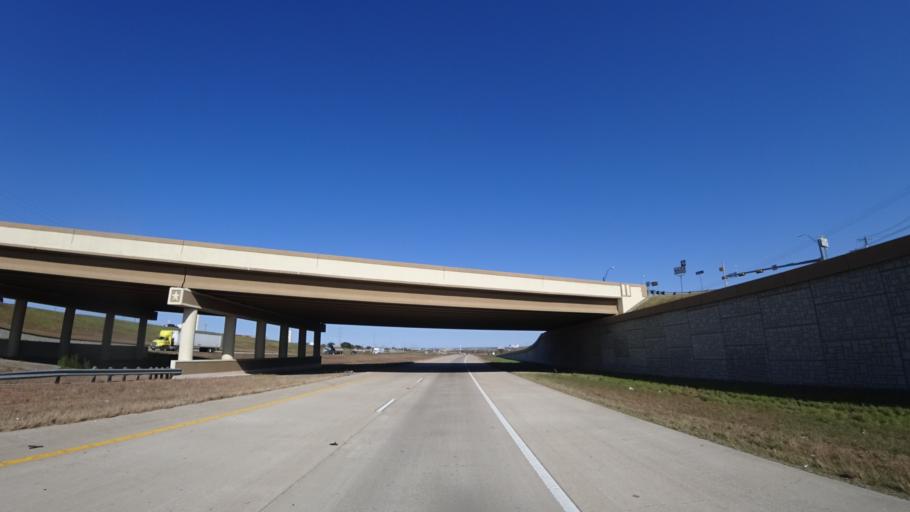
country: US
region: Texas
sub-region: Williamson County
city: Hutto
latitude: 30.5001
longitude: -97.5809
